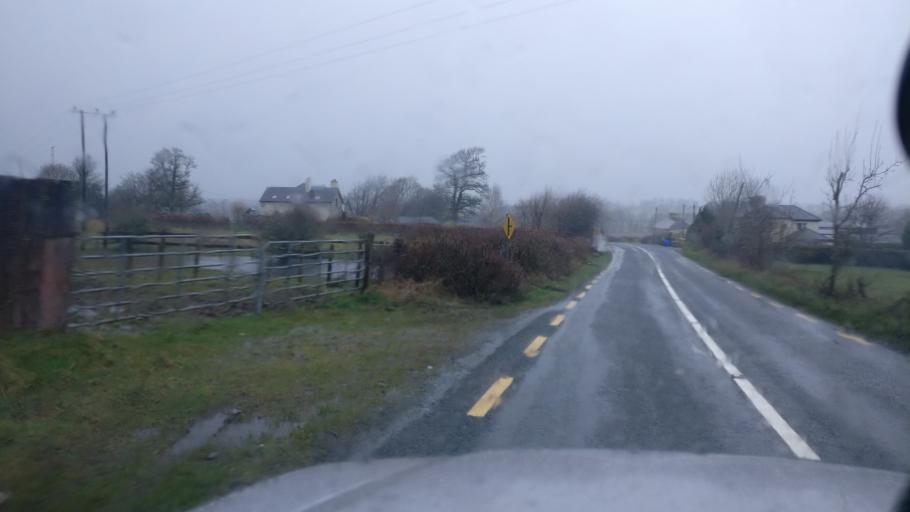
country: IE
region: Connaught
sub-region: County Galway
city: Loughrea
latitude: 53.1477
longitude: -8.4729
